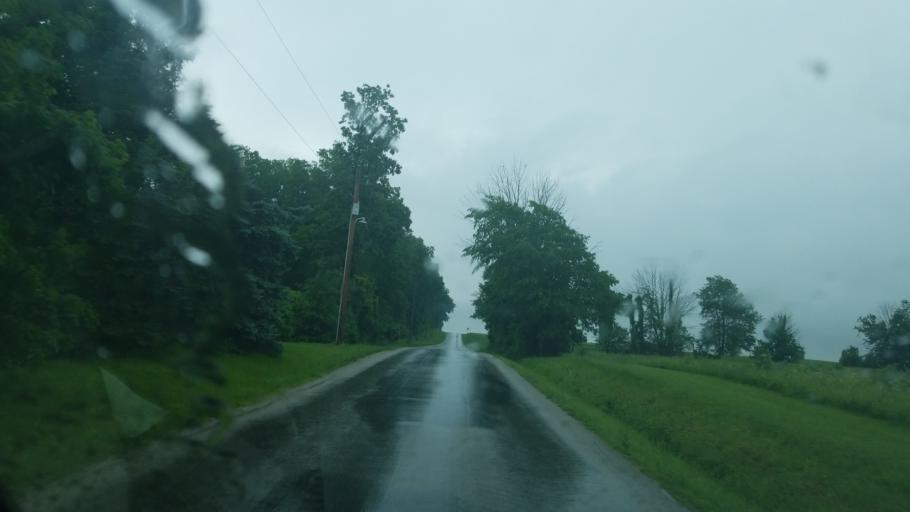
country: US
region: Ohio
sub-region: Huron County
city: Plymouth
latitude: 40.9449
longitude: -82.7085
